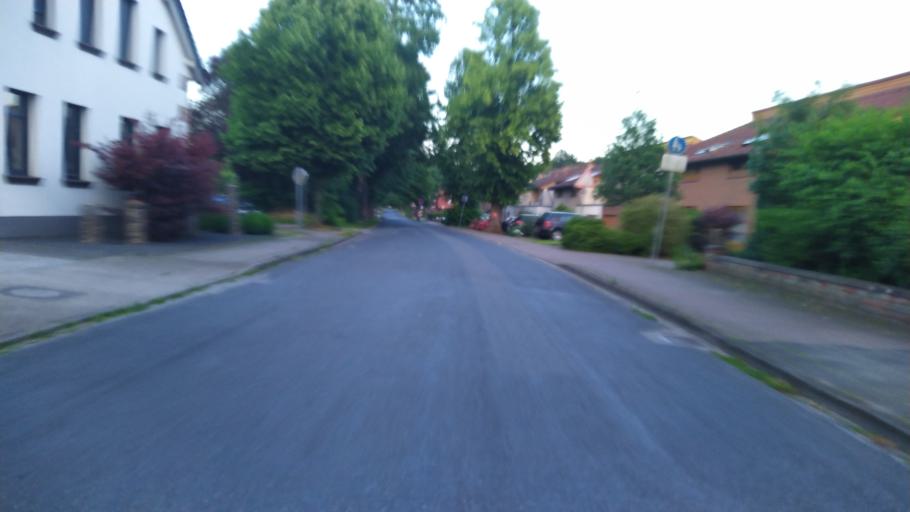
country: DE
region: Lower Saxony
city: Bremervorde
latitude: 53.4829
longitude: 9.1619
